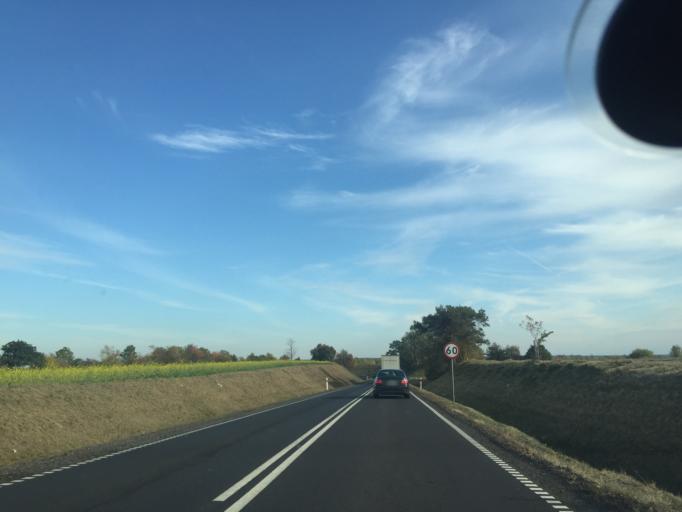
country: PL
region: Kujawsko-Pomorskie
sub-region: Powiat mogilenski
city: Mogilno
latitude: 52.6227
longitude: 18.0155
